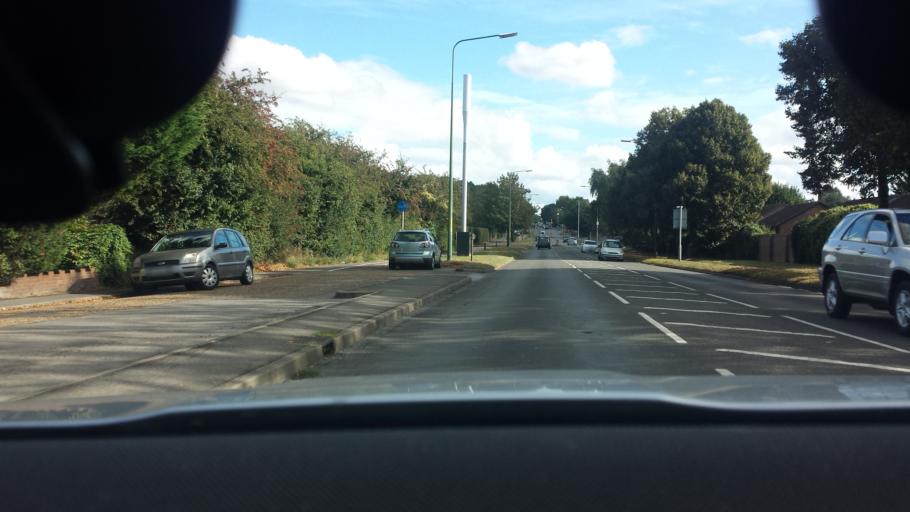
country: GB
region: England
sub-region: Kent
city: Swanley
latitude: 51.4016
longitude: 0.1654
